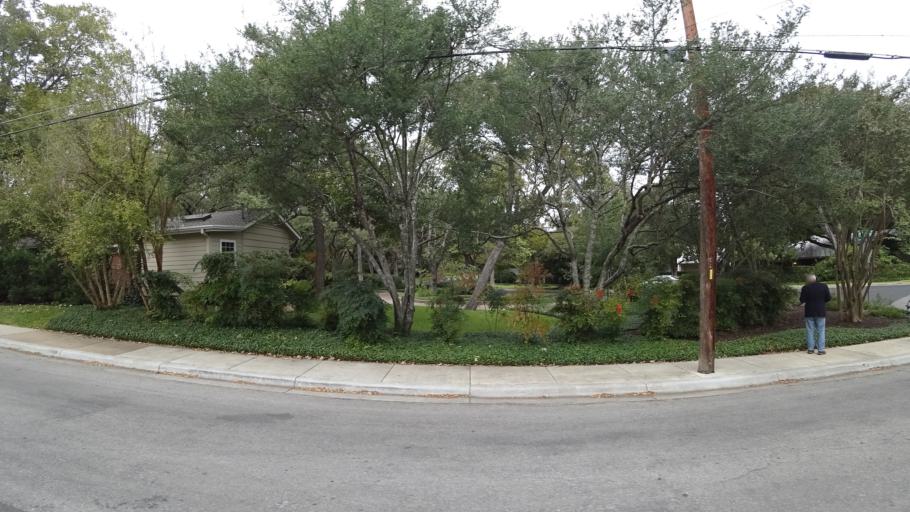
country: US
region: Texas
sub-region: Travis County
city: Rollingwood
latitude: 30.3005
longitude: -97.7686
